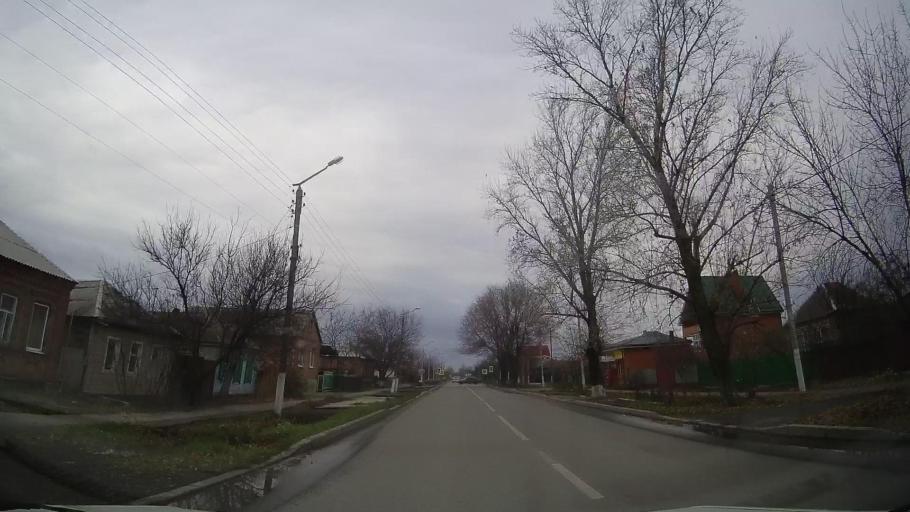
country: RU
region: Rostov
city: Bataysk
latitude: 47.1244
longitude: 39.7435
